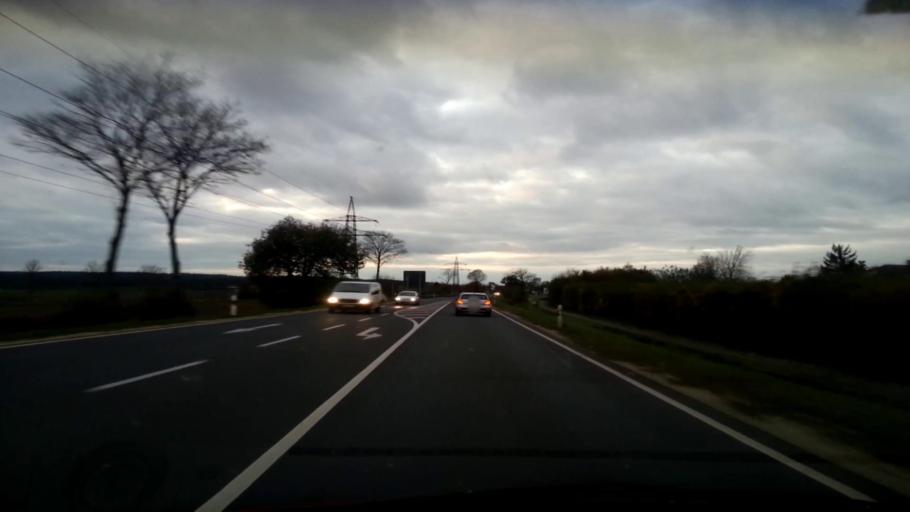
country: DE
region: Bavaria
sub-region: Upper Franconia
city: Sonnefeld
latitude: 50.2126
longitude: 11.0874
